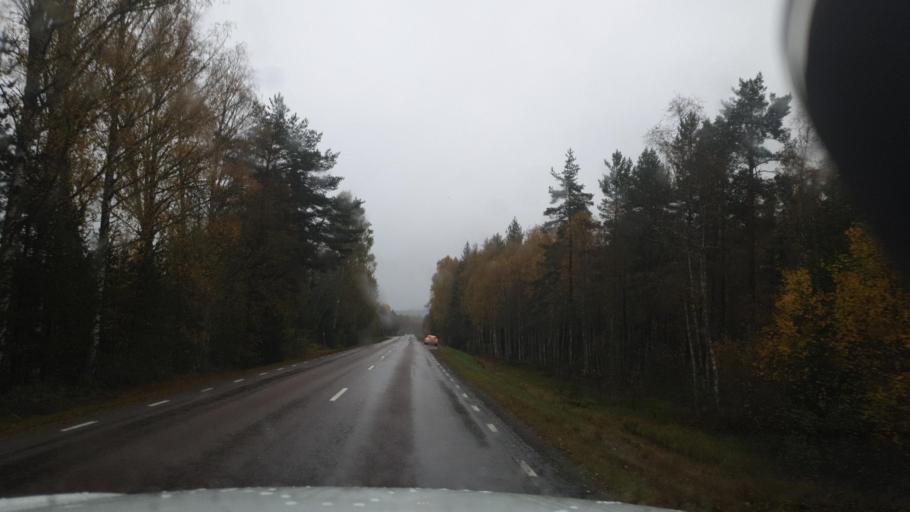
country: SE
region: Vaermland
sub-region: Eda Kommun
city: Charlottenberg
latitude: 59.7977
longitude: 12.2457
